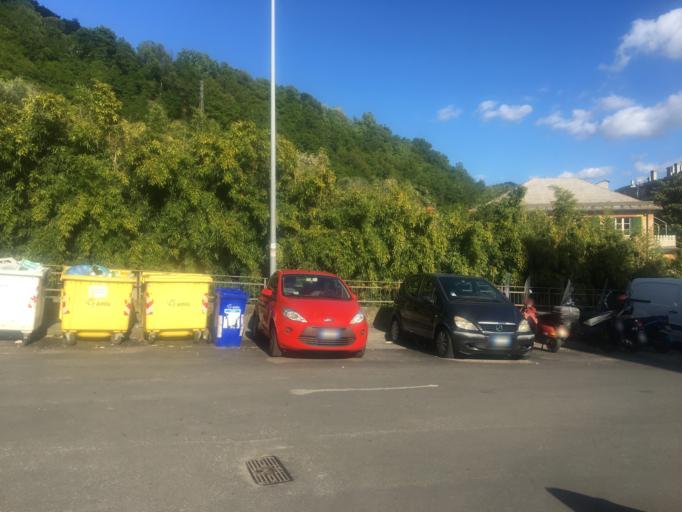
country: IT
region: Liguria
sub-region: Provincia di Genova
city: Piccarello
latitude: 44.4557
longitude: 8.9852
